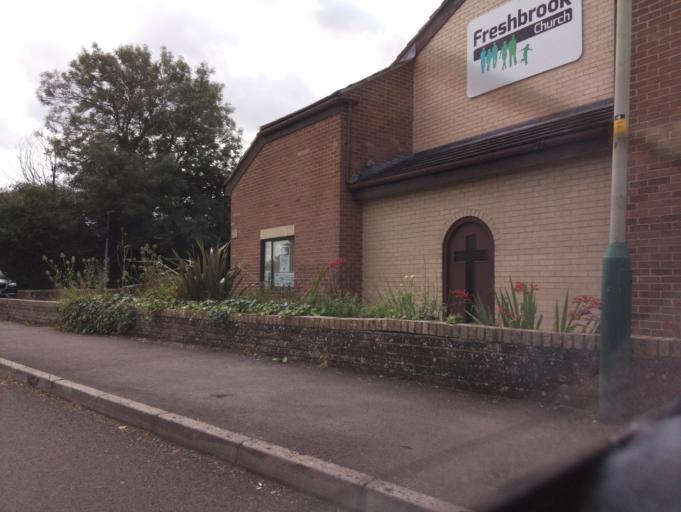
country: GB
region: England
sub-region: Wiltshire
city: Lydiard Tregoze
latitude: 51.5489
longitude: -1.8396
